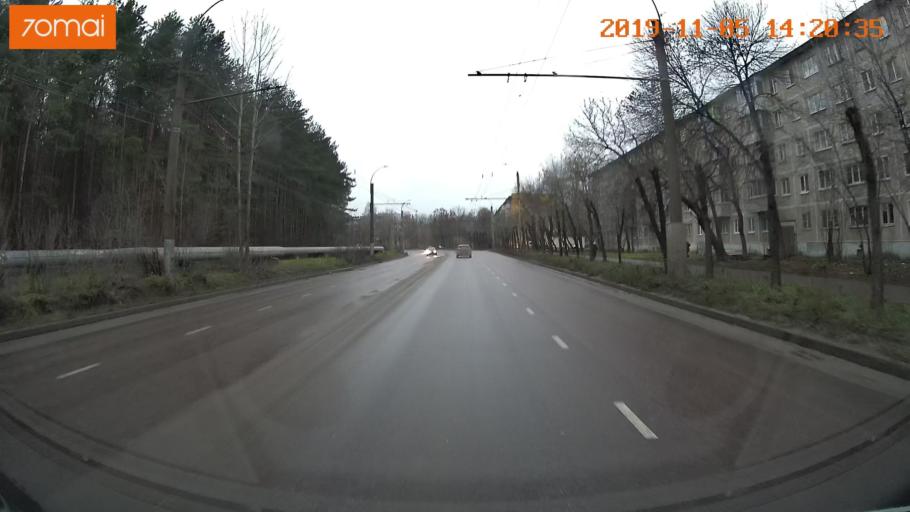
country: RU
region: Ivanovo
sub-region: Gorod Ivanovo
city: Ivanovo
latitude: 56.9577
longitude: 41.0195
